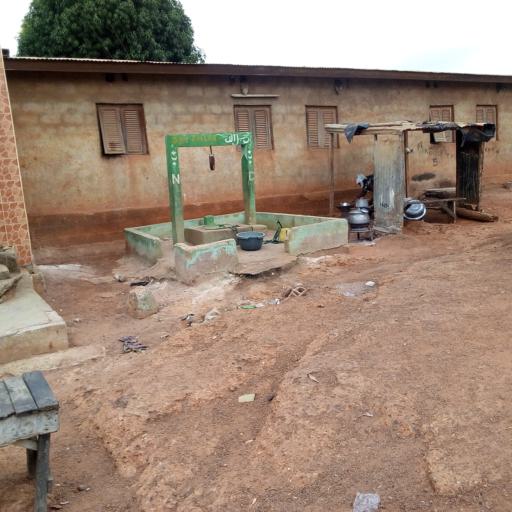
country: CI
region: Vallee du Bandama
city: Bouake
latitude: 7.6948
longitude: -5.0160
